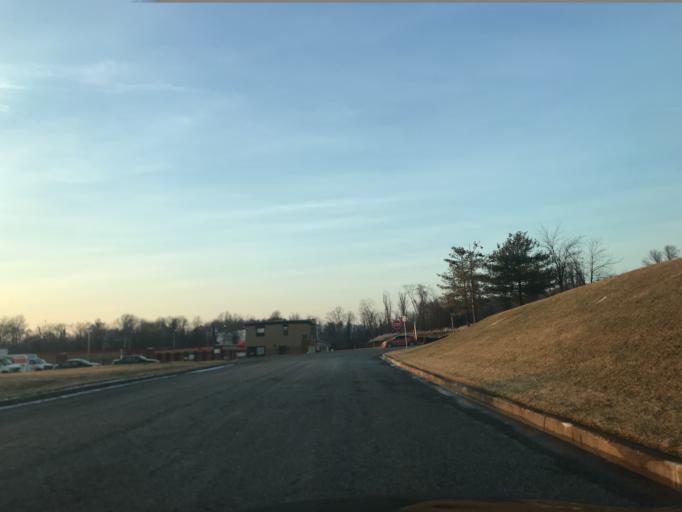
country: US
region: Maryland
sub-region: Harford County
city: Edgewood
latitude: 39.4522
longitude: -76.3136
